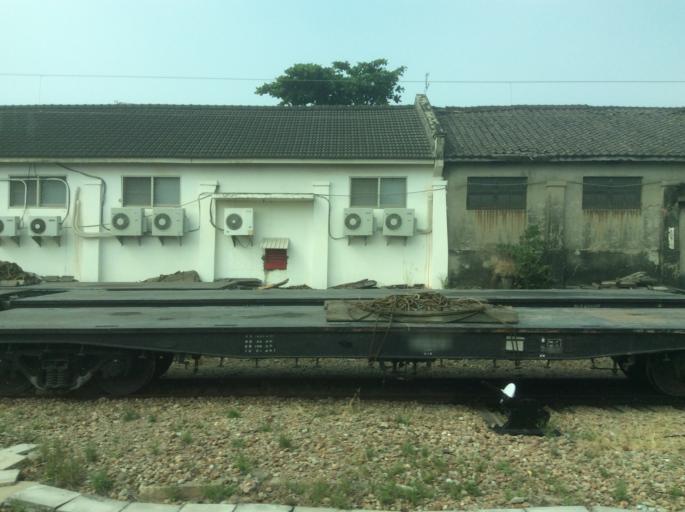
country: TW
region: Taiwan
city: Xinying
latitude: 23.3083
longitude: 120.3242
